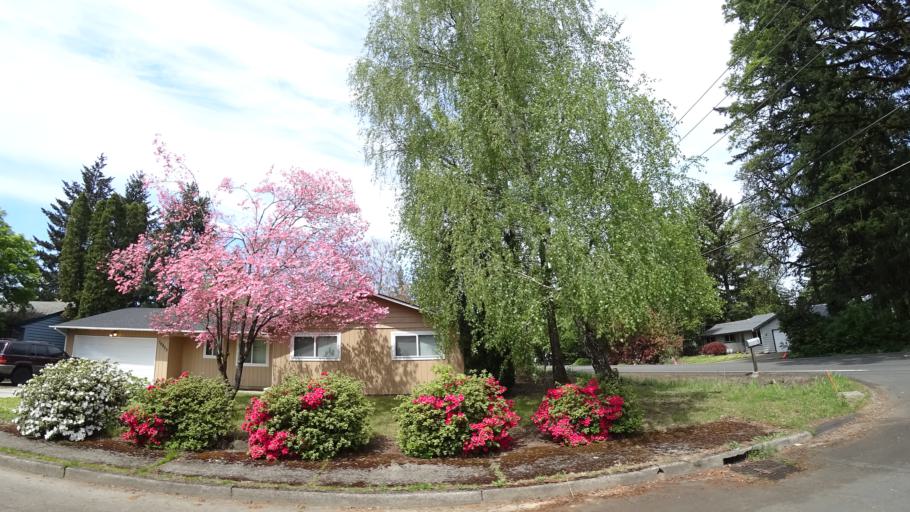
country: US
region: Oregon
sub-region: Washington County
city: Aloha
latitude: 45.4797
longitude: -122.8819
